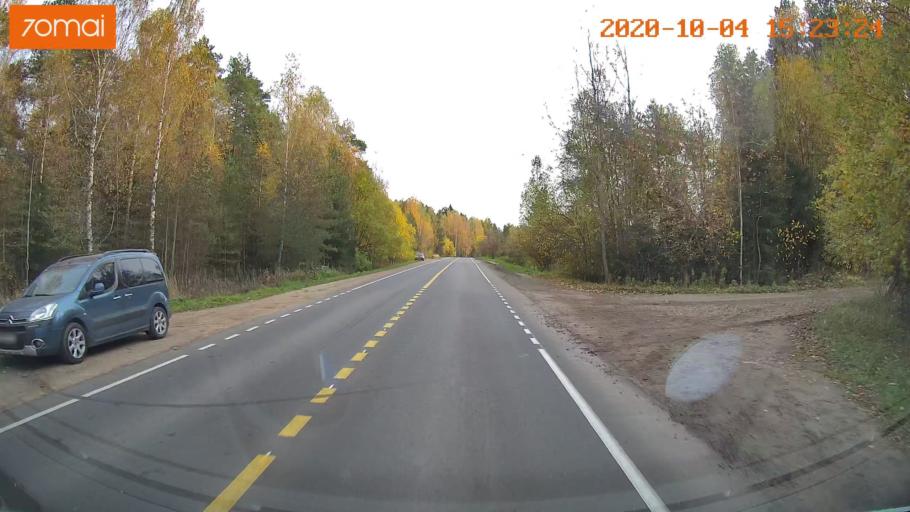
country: RU
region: Ivanovo
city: Bogorodskoye
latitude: 57.0739
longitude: 40.9487
